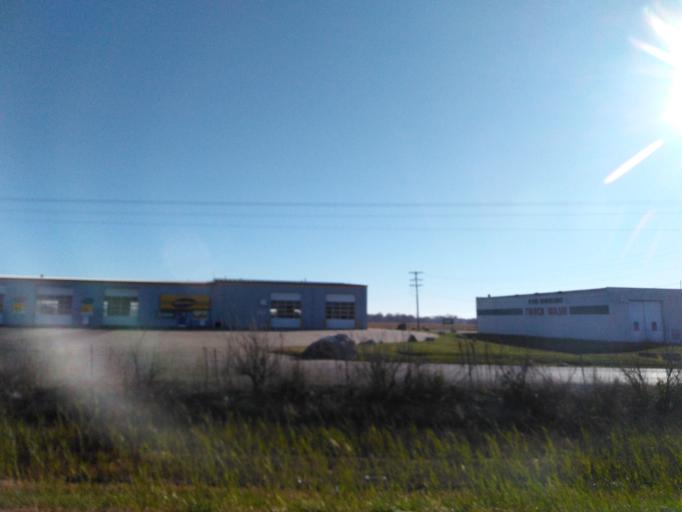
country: US
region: Illinois
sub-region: Madison County
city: Troy
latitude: 38.7389
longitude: -89.9106
